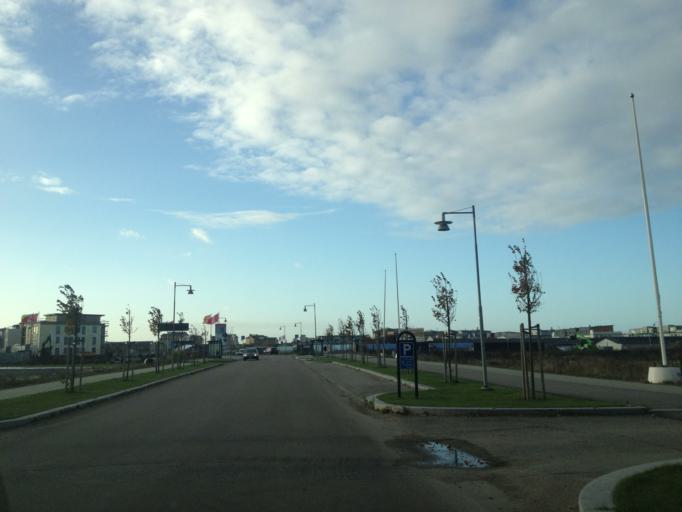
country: SE
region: Skane
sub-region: Lomma Kommun
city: Lomma
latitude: 55.6795
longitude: 13.0670
